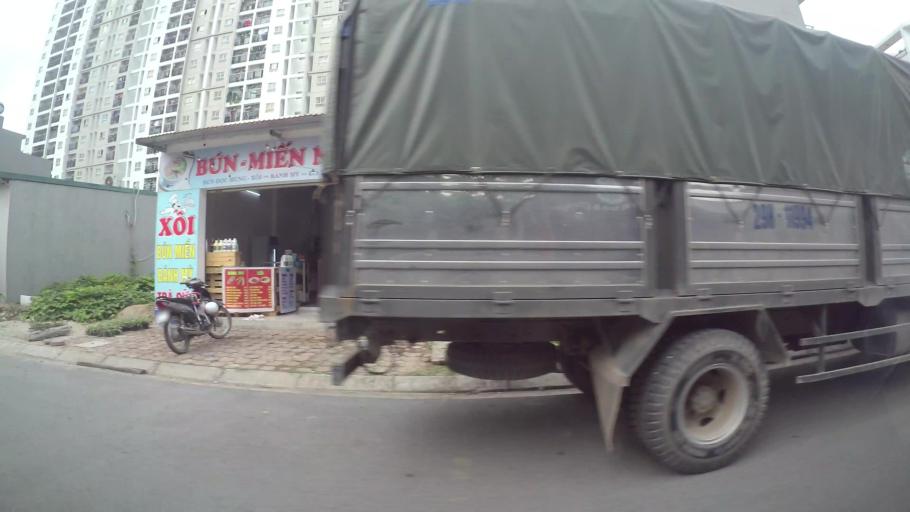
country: VN
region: Ha Noi
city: Trau Quy
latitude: 21.0416
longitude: 105.9277
